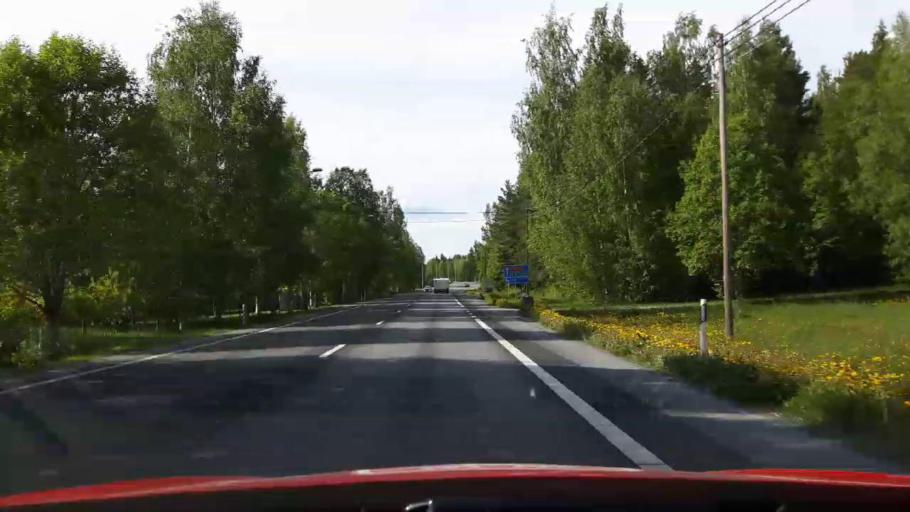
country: SE
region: Jaemtland
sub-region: OEstersunds Kommun
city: Brunflo
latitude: 63.1215
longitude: 14.7958
